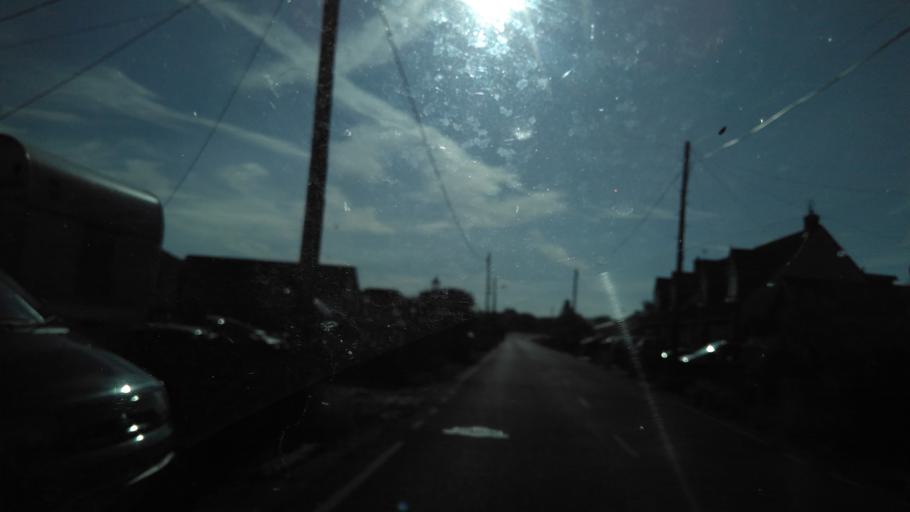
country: GB
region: England
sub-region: Kent
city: Whitstable
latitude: 51.3463
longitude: 0.9855
